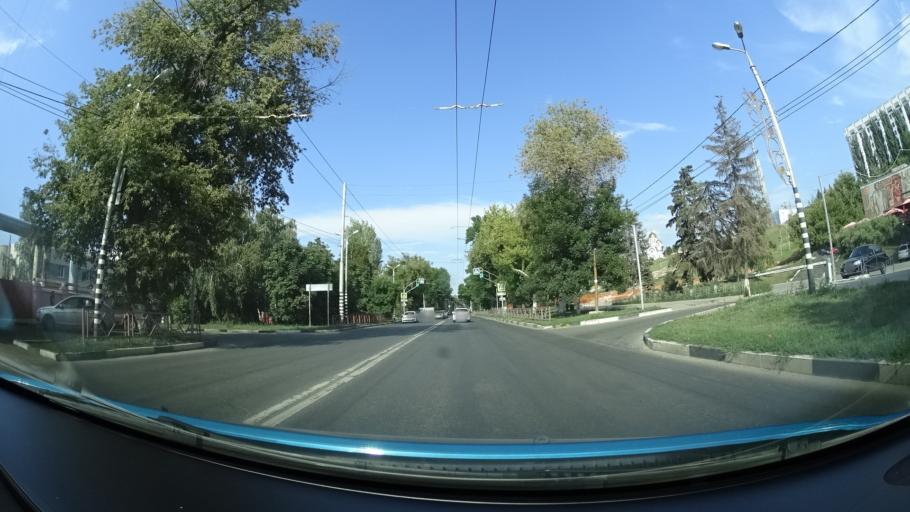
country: RU
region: Samara
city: Samara
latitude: 53.2040
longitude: 50.1060
